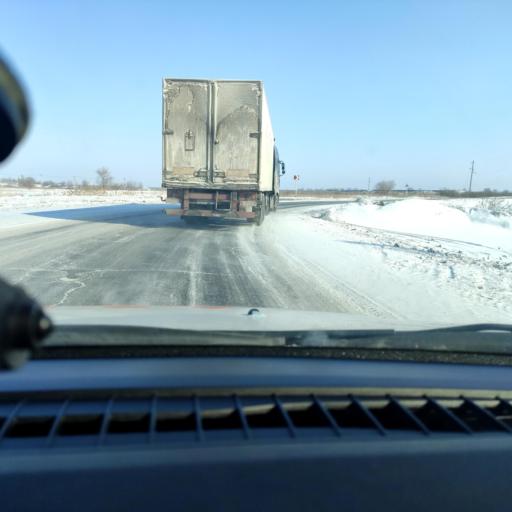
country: RU
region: Samara
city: Smyshlyayevka
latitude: 53.1835
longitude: 50.4772
